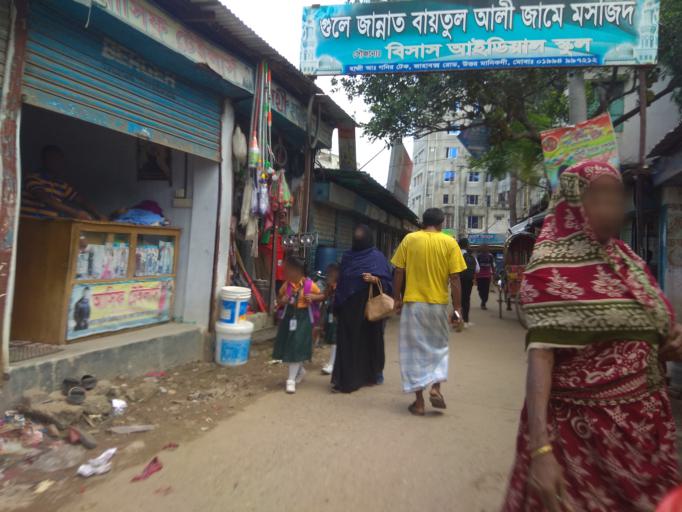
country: BD
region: Dhaka
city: Tungi
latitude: 23.8267
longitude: 90.3915
